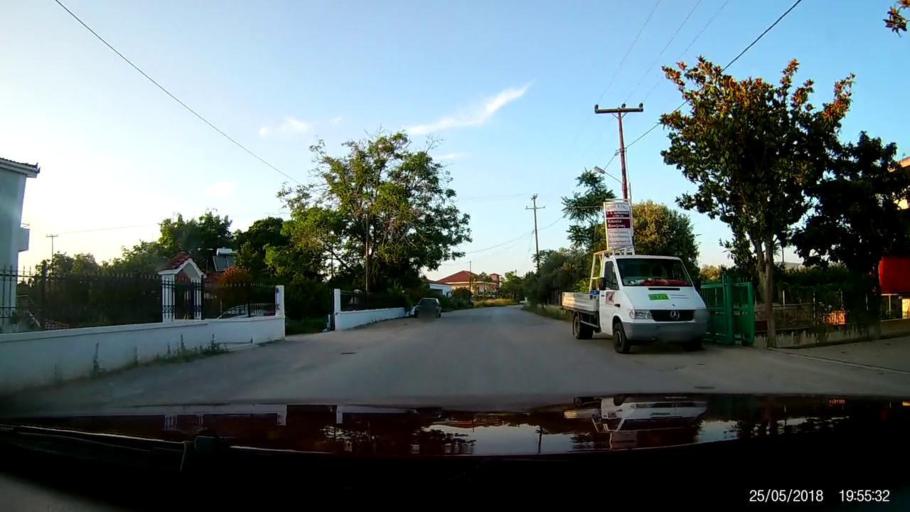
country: GR
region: Central Greece
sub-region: Nomos Evvoias
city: Ayios Nikolaos
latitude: 38.4257
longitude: 23.6588
